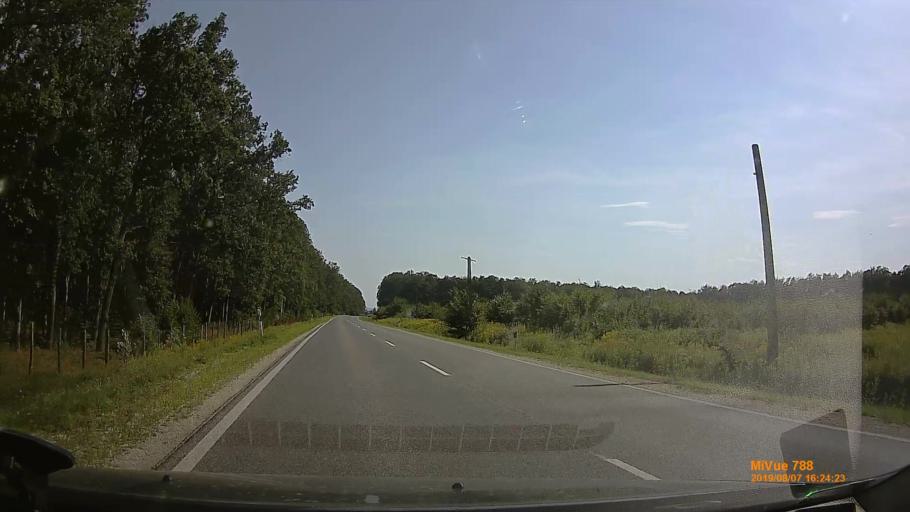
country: HU
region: Zala
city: Lenti
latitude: 46.7367
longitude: 16.5533
